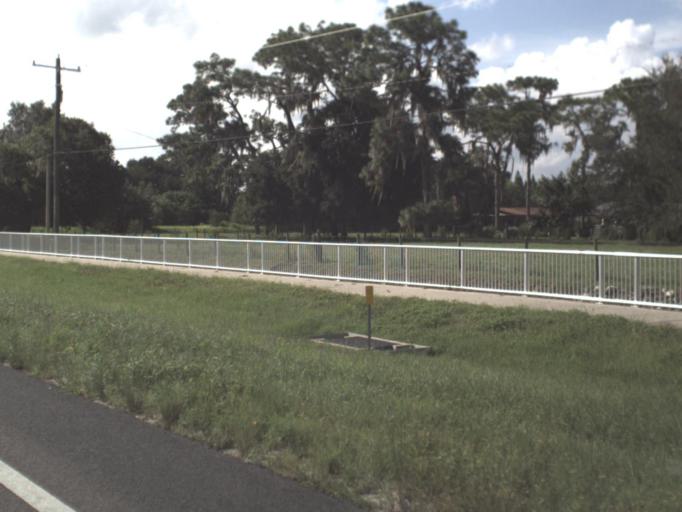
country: US
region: Florida
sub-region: Sarasota County
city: The Meadows
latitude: 27.4756
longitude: -82.3937
